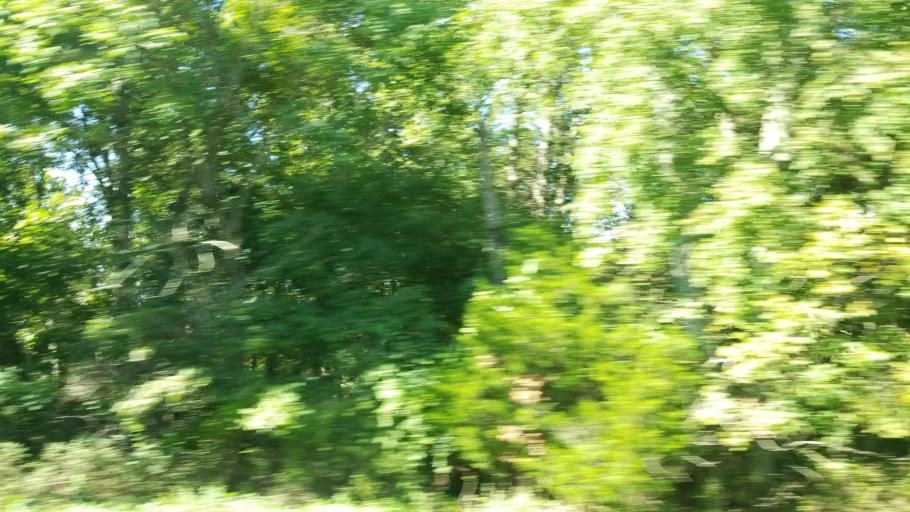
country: US
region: Illinois
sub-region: Saline County
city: Carrier Mills
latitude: 37.7953
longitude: -88.7497
